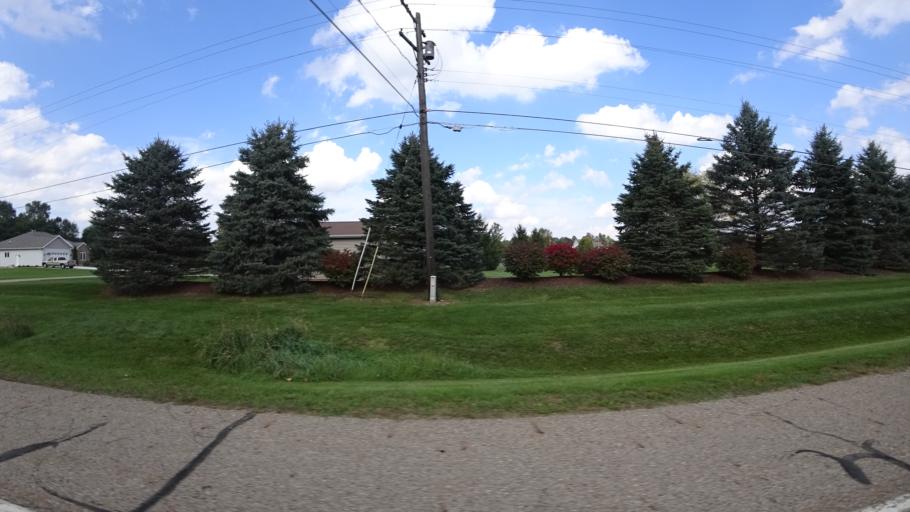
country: US
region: Michigan
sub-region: Branch County
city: Union City
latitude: 42.1060
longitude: -85.0656
